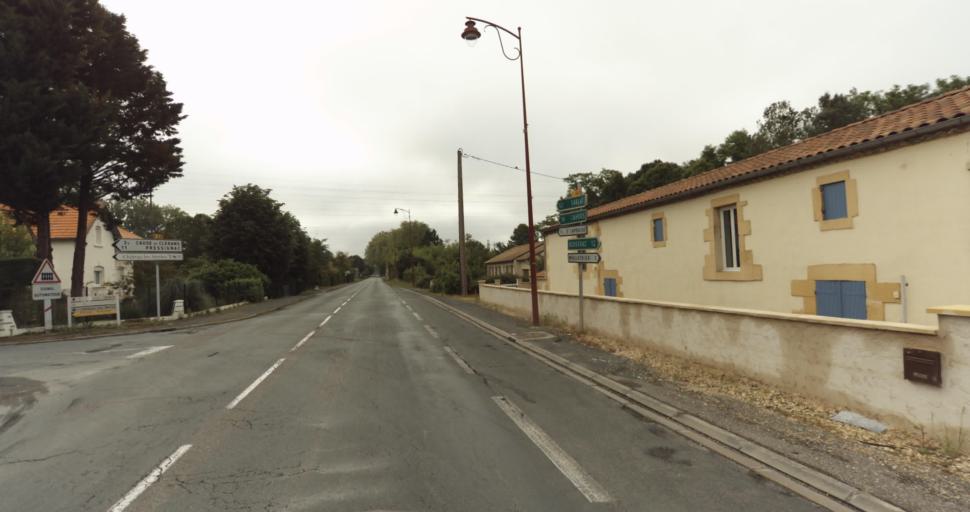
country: FR
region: Aquitaine
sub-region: Departement de la Dordogne
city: Mouleydier
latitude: 44.8475
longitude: 0.6320
